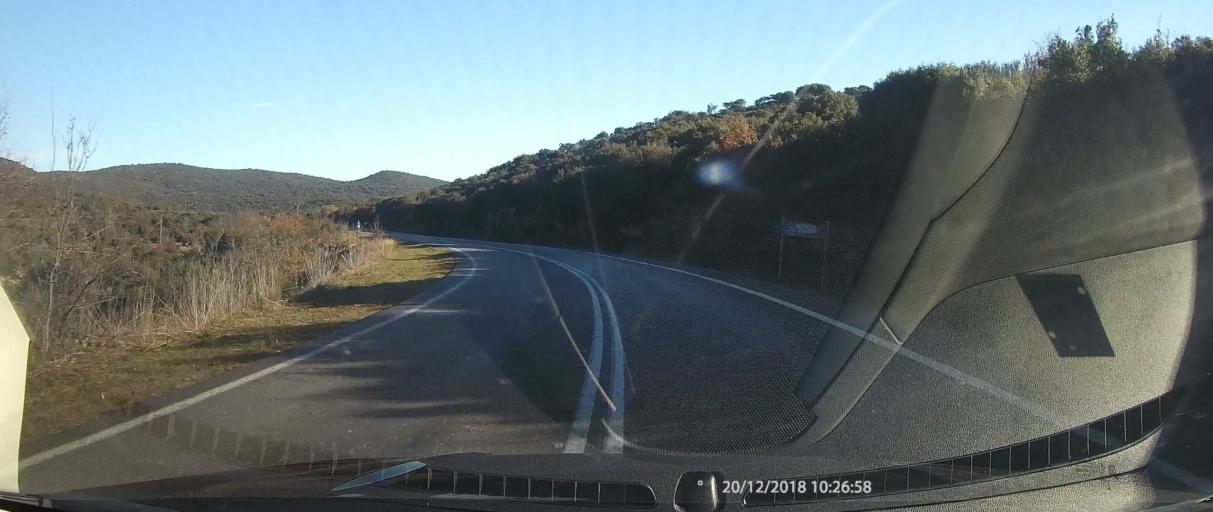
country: GR
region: Peloponnese
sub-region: Nomos Lakonias
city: Kariai
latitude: 37.2384
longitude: 22.4370
